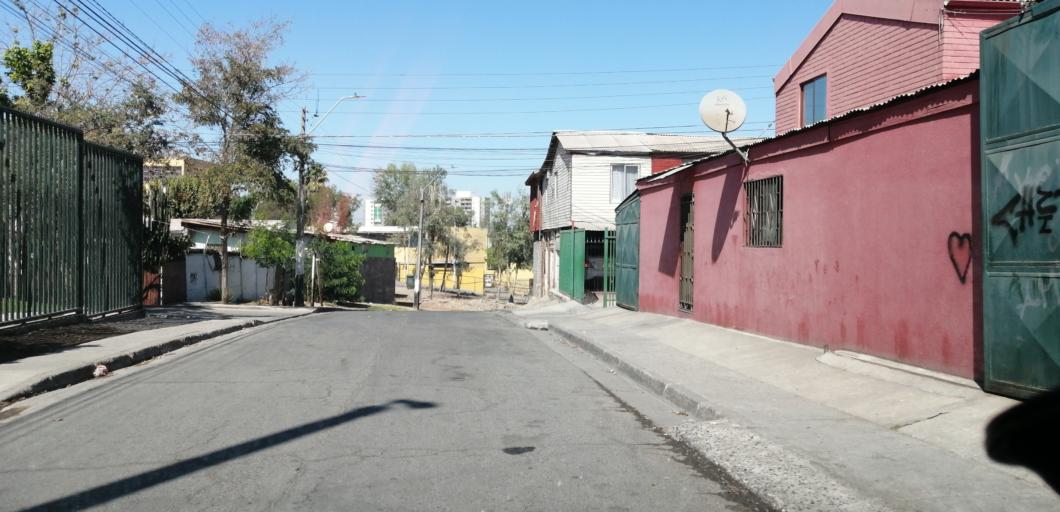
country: CL
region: Santiago Metropolitan
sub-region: Provincia de Santiago
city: Lo Prado
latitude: -33.4460
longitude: -70.7587
